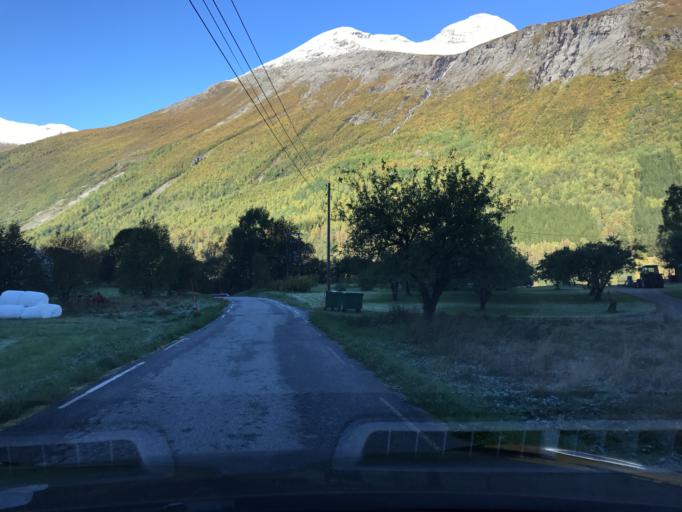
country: NO
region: More og Romsdal
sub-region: Norddal
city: Valldal
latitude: 62.3138
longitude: 7.3023
